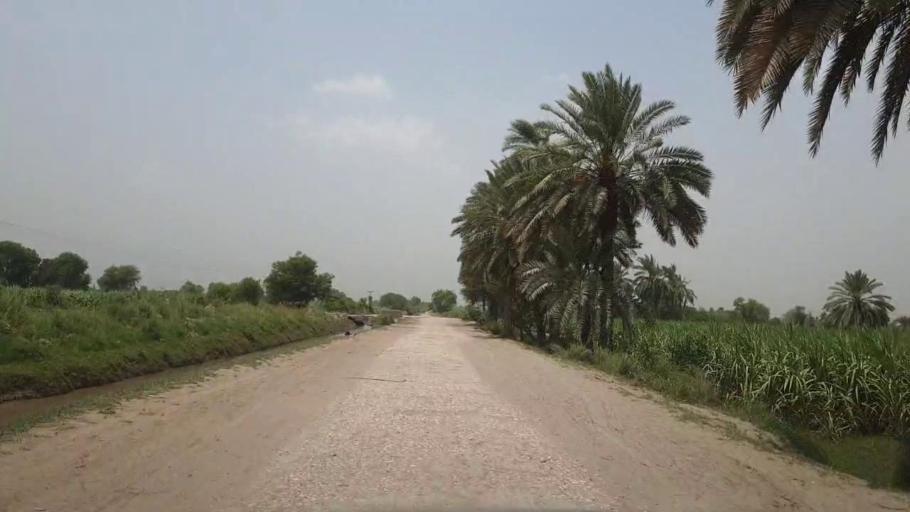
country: PK
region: Sindh
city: Sobhadero
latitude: 27.4363
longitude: 68.3995
